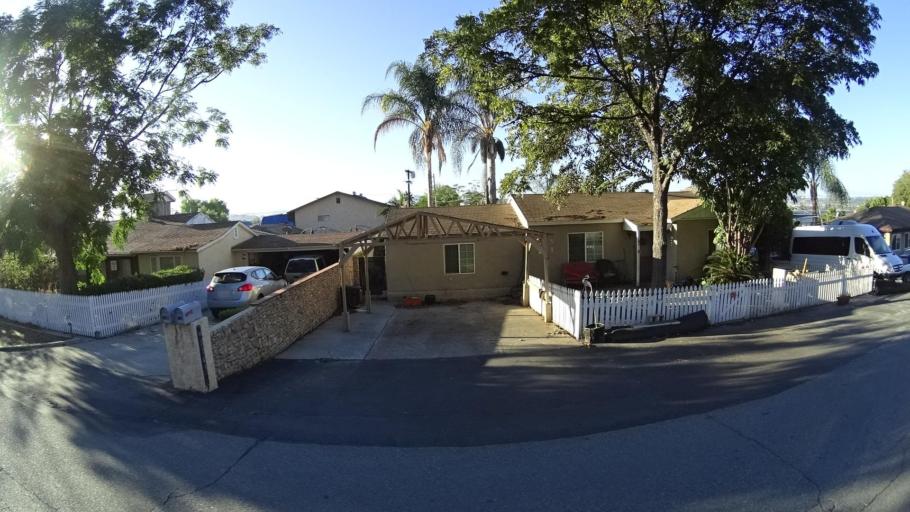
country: US
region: California
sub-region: San Diego County
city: Bostonia
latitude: 32.8144
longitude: -116.9425
